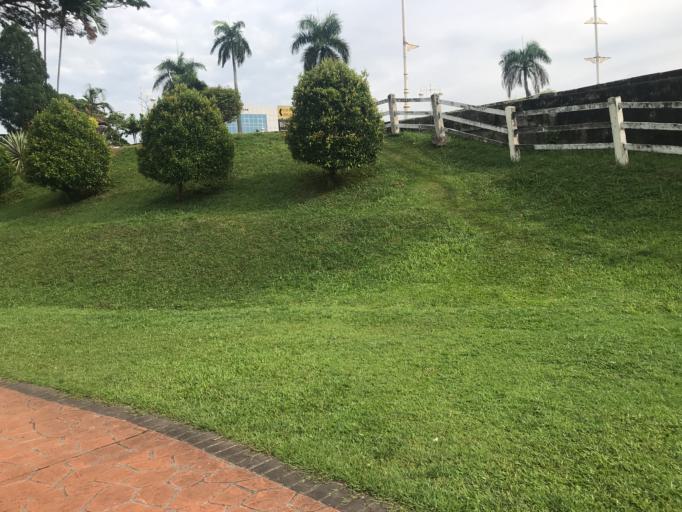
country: MY
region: Perak
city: Ipoh
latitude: 4.6000
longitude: 101.0761
